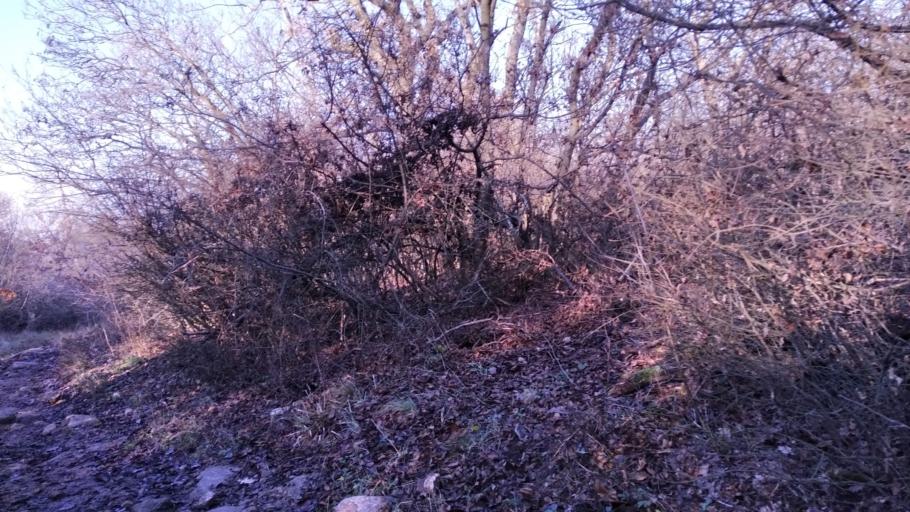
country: HU
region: Pest
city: Urom
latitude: 47.5524
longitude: 18.9909
